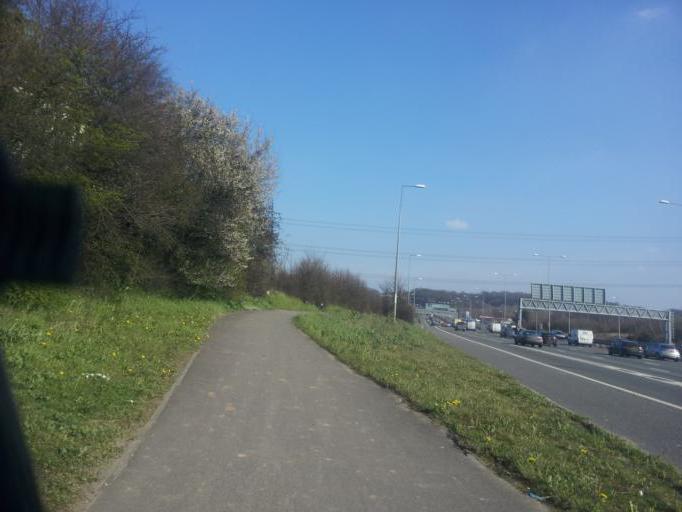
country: GB
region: England
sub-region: Kent
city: Gravesend
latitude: 51.4077
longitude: 0.3894
